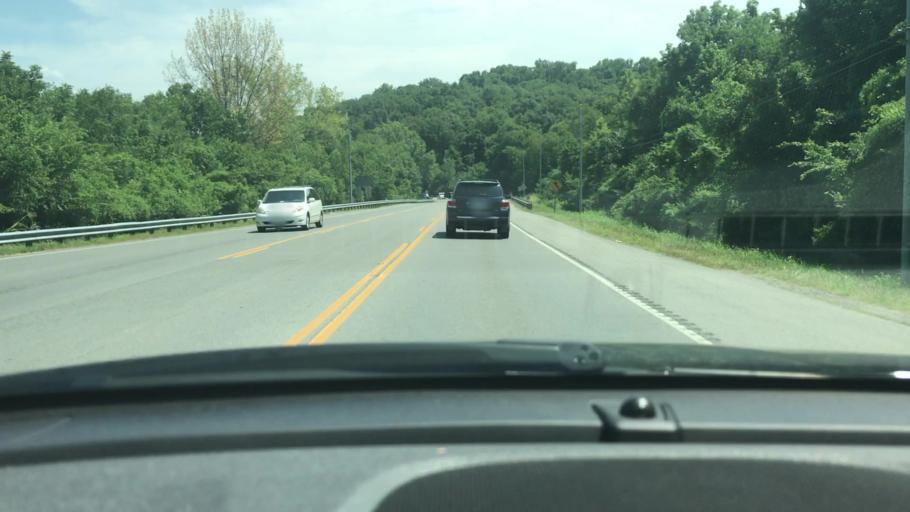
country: US
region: Tennessee
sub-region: Sumner County
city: Shackle Island
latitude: 36.3699
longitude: -86.6166
